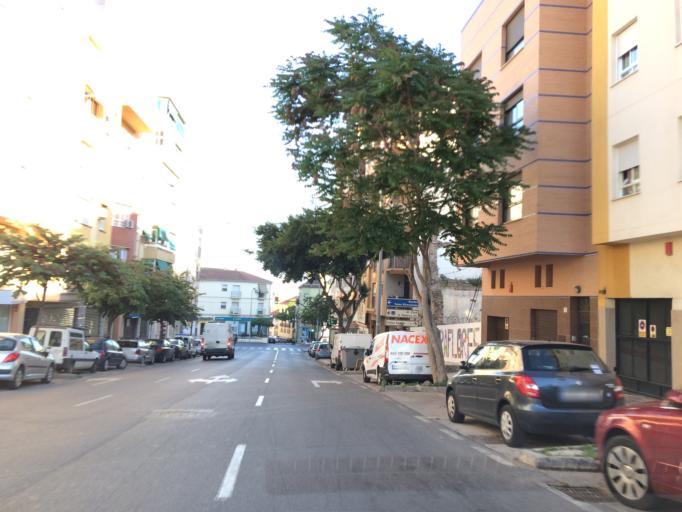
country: ES
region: Andalusia
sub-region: Provincia de Malaga
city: Malaga
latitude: 36.7253
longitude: -4.4322
